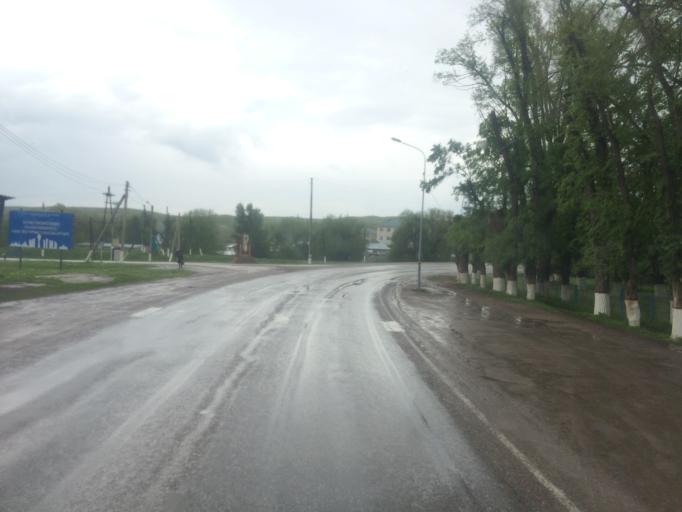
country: KZ
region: Zhambyl
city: Georgiyevka
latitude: 43.2343
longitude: 74.7595
